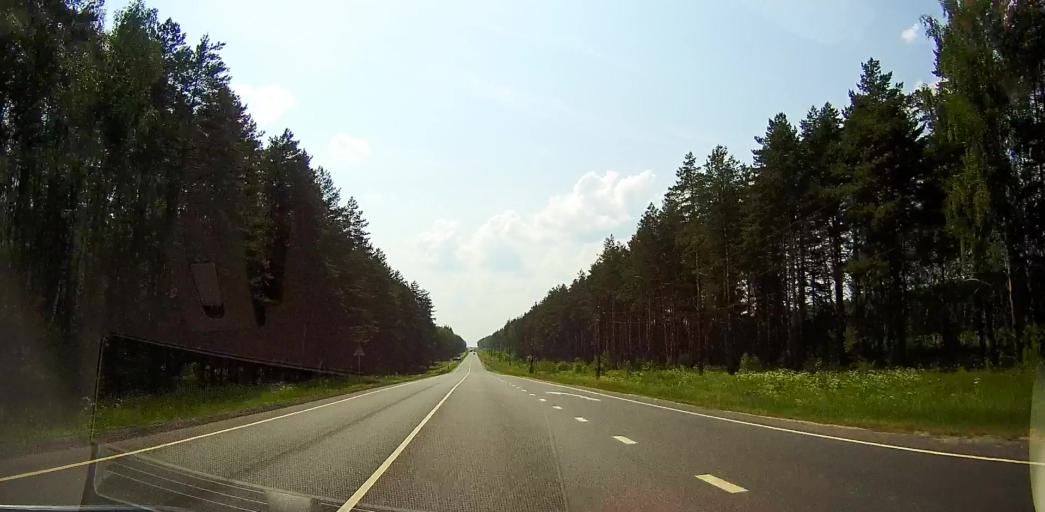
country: RU
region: Moskovskaya
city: Meshcherino
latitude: 55.1718
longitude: 38.3299
